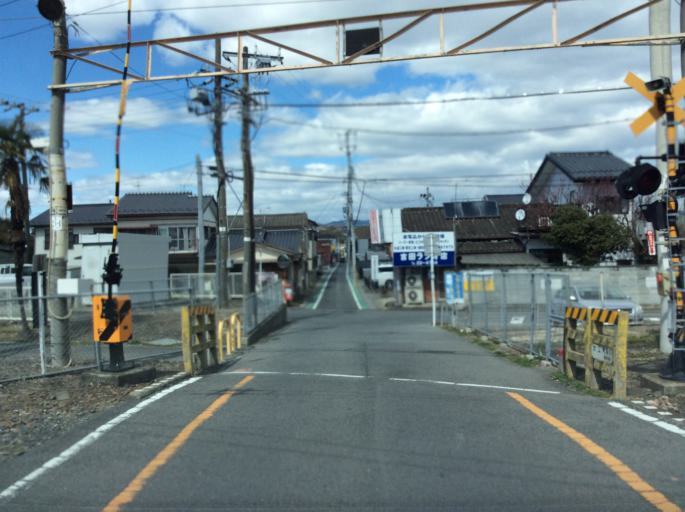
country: JP
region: Fukushima
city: Iwaki
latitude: 37.0584
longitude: 140.8962
